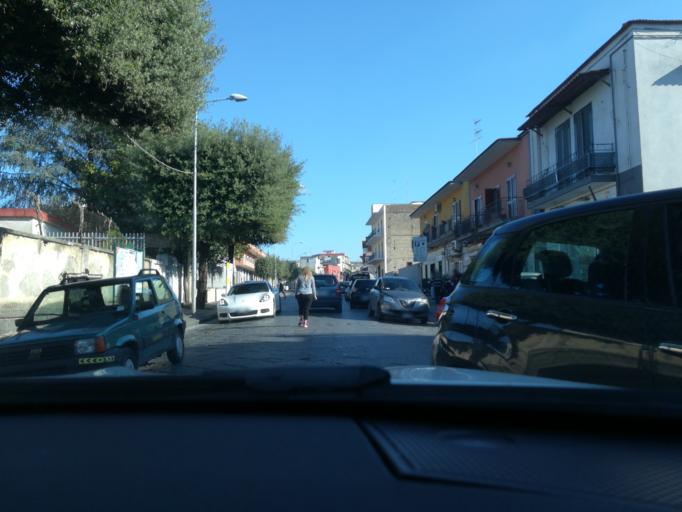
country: IT
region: Campania
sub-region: Provincia di Napoli
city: Sant'Anastasia
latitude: 40.8702
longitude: 14.3928
